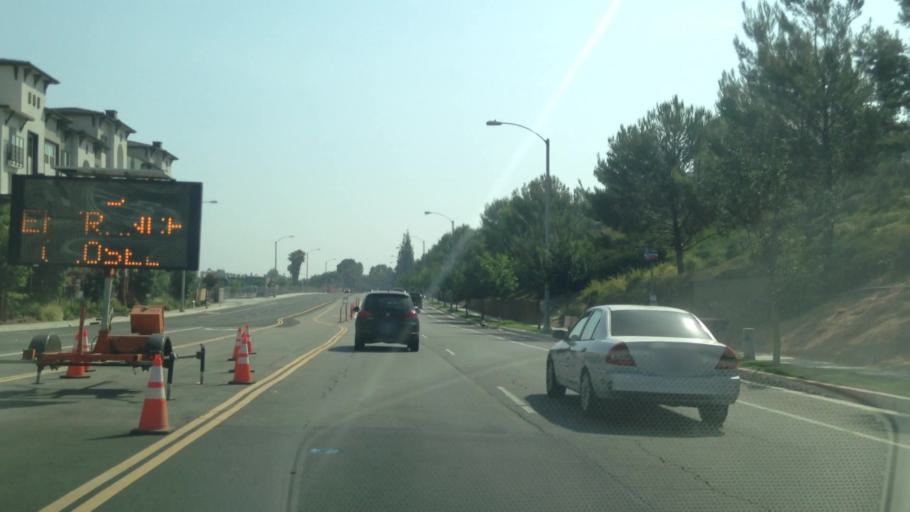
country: US
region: California
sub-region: Riverside County
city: Home Gardens
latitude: 33.8984
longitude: -117.4690
